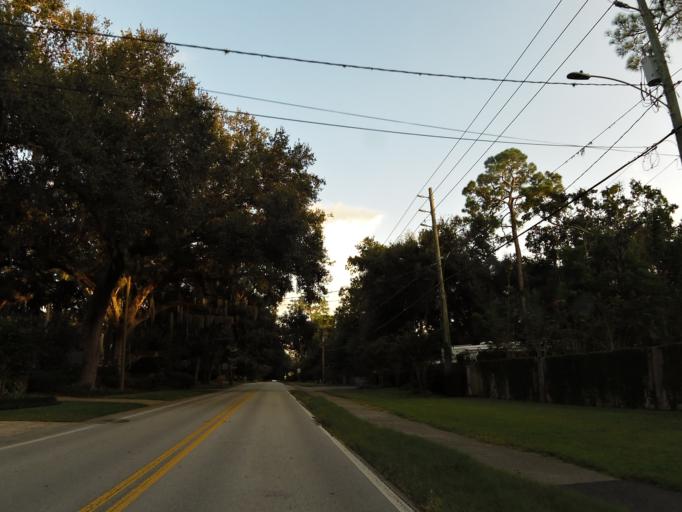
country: US
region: Florida
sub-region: Clay County
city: Orange Park
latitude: 30.1977
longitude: -81.6327
